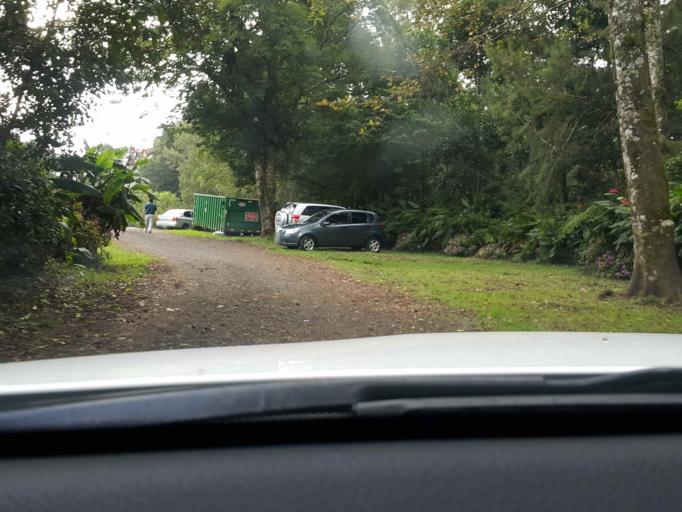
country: CR
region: Heredia
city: San Josecito
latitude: 10.0679
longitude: -84.0759
